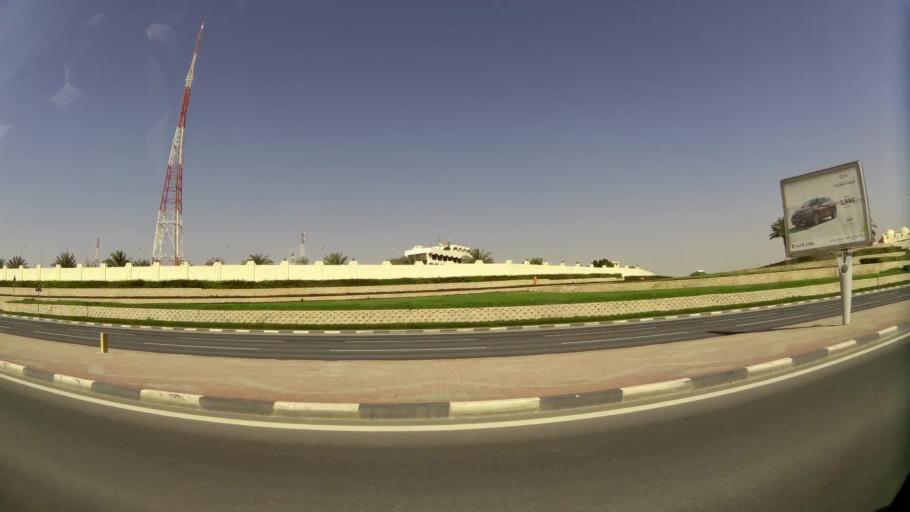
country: QA
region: Baladiyat ad Dawhah
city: Doha
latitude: 25.3129
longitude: 51.5054
